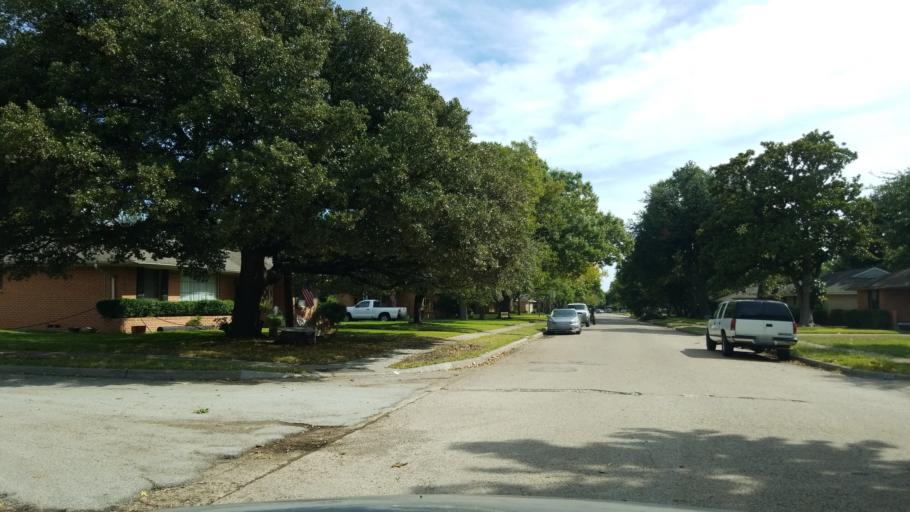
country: US
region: Texas
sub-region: Dallas County
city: Garland
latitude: 32.8996
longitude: -96.6622
